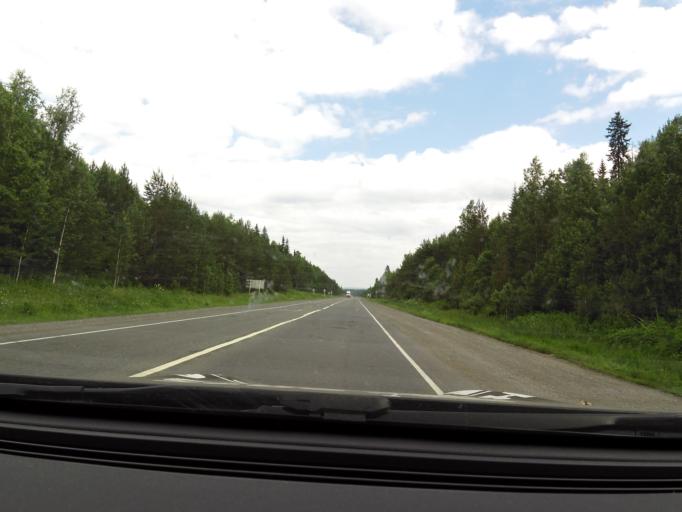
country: RU
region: Sverdlovsk
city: Druzhinino
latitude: 56.7961
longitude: 59.4180
